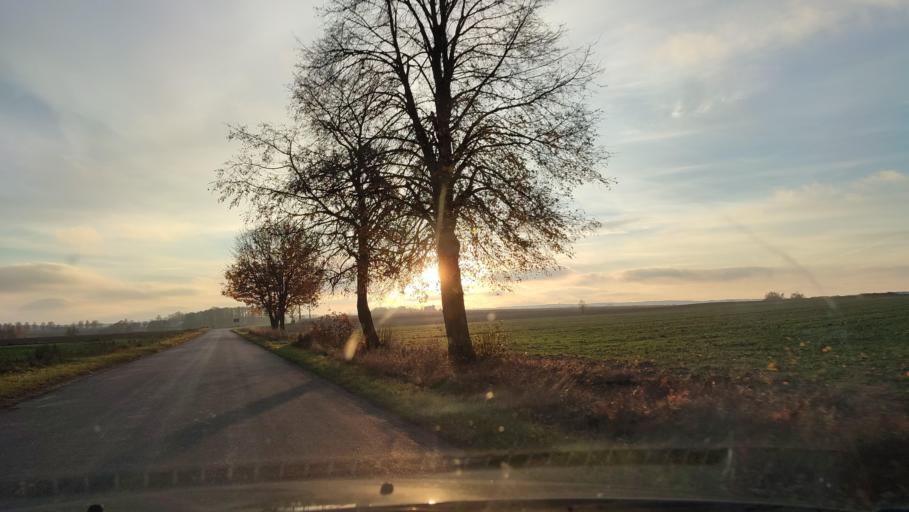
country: PL
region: Masovian Voivodeship
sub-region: Powiat mlawski
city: Wieczfnia Koscielna
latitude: 53.2306
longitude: 20.5489
